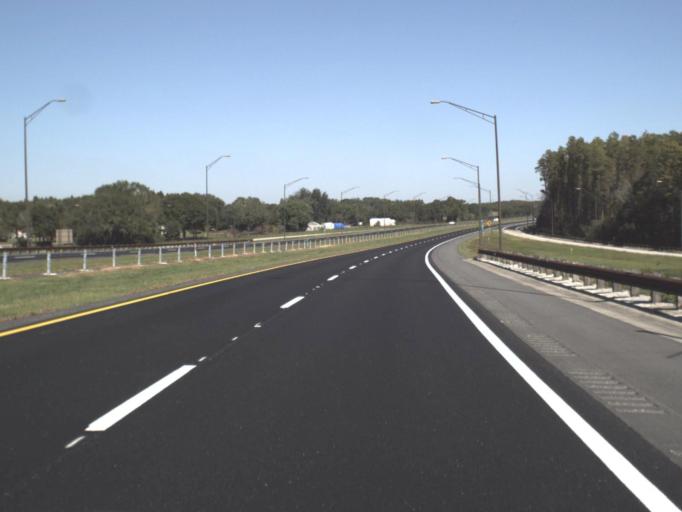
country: US
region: Florida
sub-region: Hillsborough County
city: Greater Northdale
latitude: 28.1305
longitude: -82.5484
